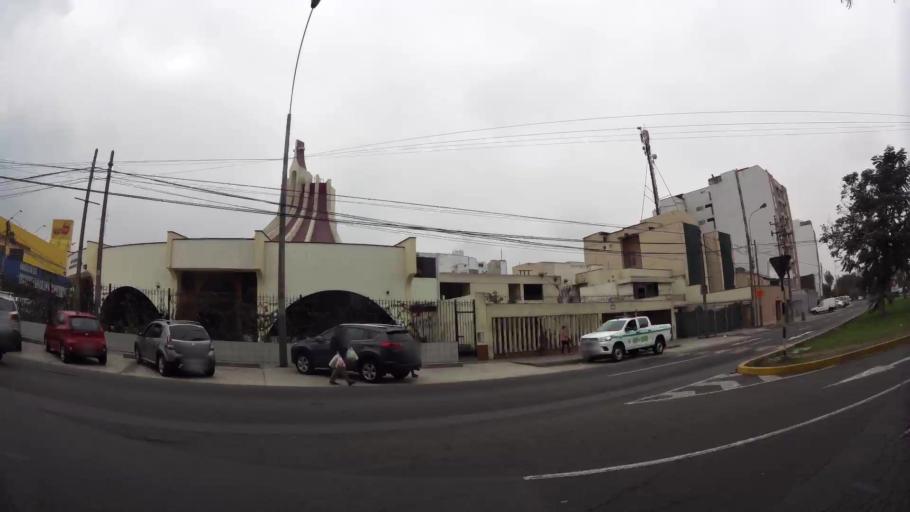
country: PE
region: Lima
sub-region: Lima
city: San Luis
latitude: -12.0989
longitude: -77.0121
